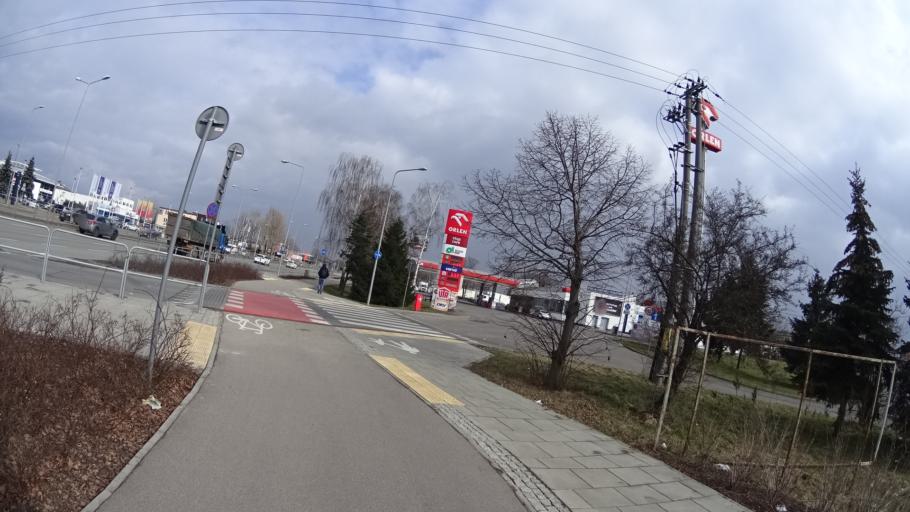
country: PL
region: Masovian Voivodeship
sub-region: Warszawa
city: Ursus
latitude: 52.2162
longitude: 20.8805
